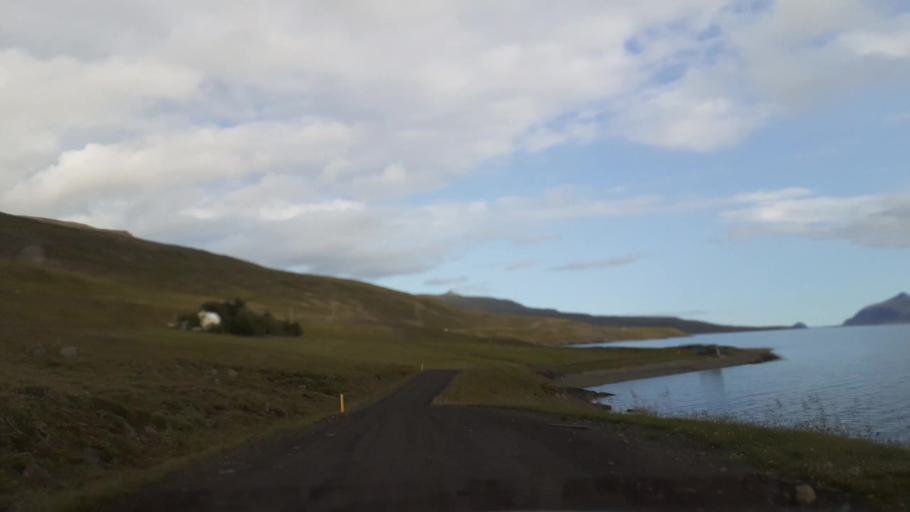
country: IS
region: East
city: Eskifjoerdur
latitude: 65.0382
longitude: -13.8799
